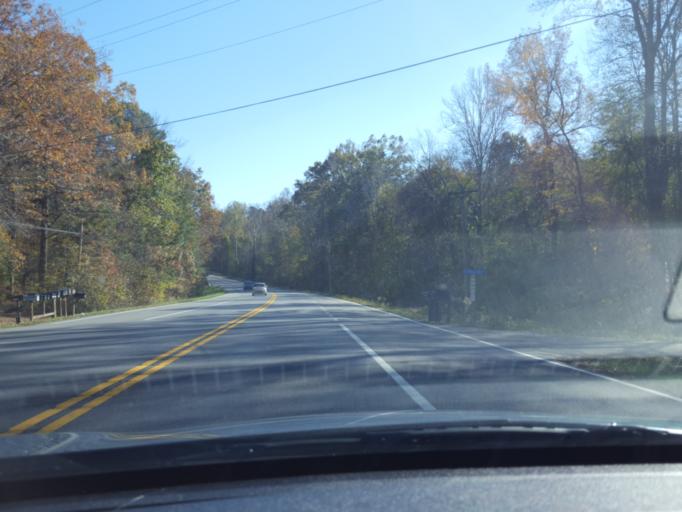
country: US
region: Maryland
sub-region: Saint Mary's County
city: Leonardtown
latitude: 38.2615
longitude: -76.6038
